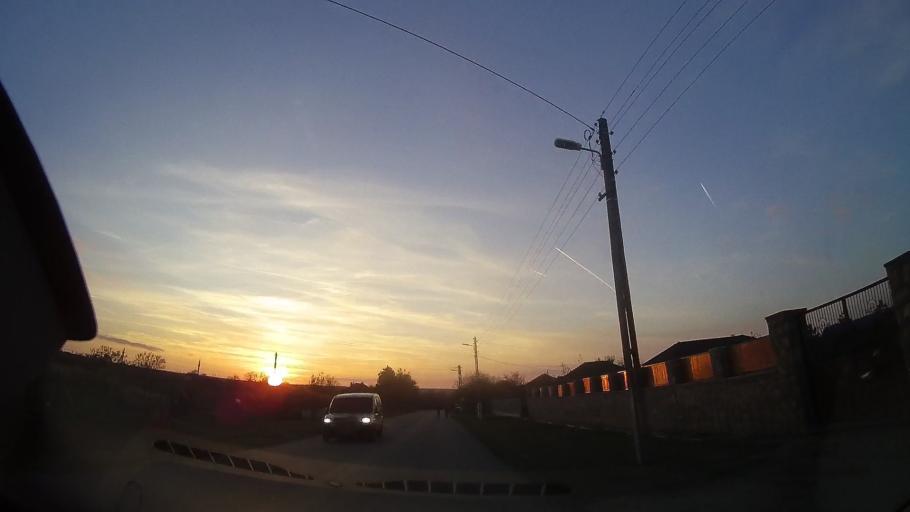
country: RO
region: Constanta
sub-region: Comuna Mereni
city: Mereni
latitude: 44.0154
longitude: 28.3292
